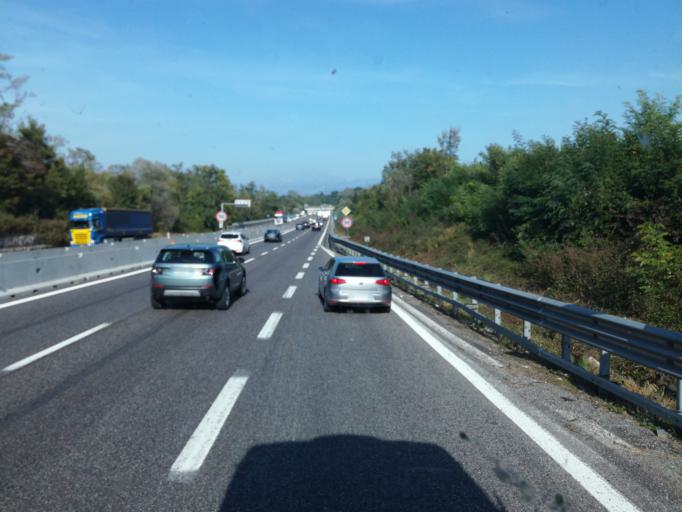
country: IT
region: Lombardy
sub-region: Provincia di Monza e Brianza
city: Briosco
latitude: 45.7164
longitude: 9.2299
